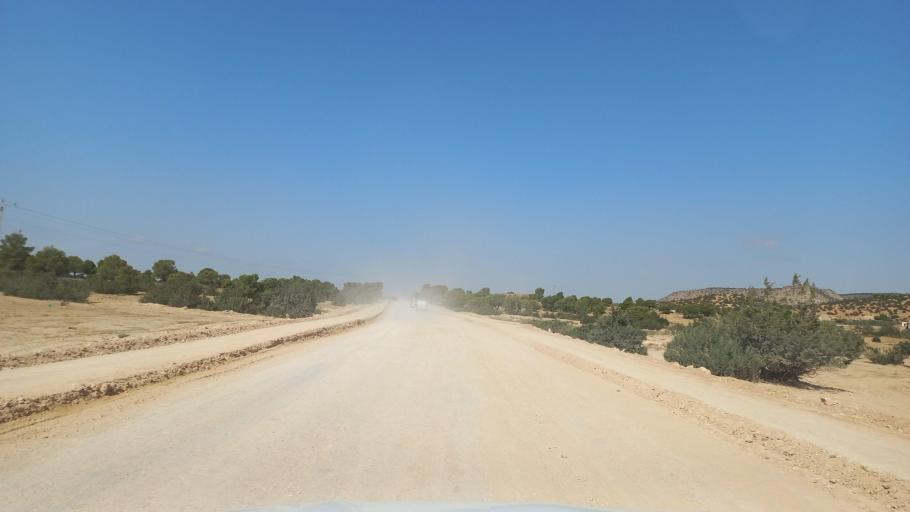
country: TN
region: Al Qasrayn
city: Sbiba
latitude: 35.4050
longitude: 8.9930
